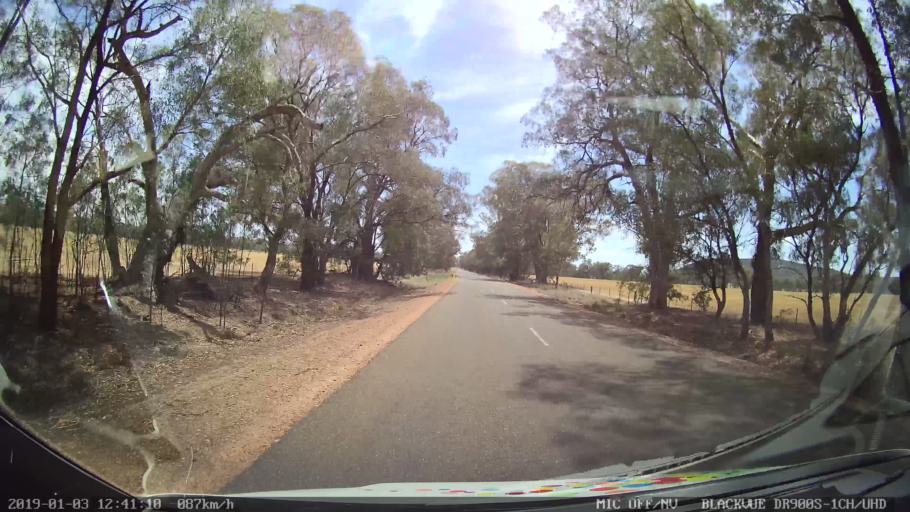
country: AU
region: New South Wales
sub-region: Weddin
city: Grenfell
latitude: -33.8032
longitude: 148.2146
